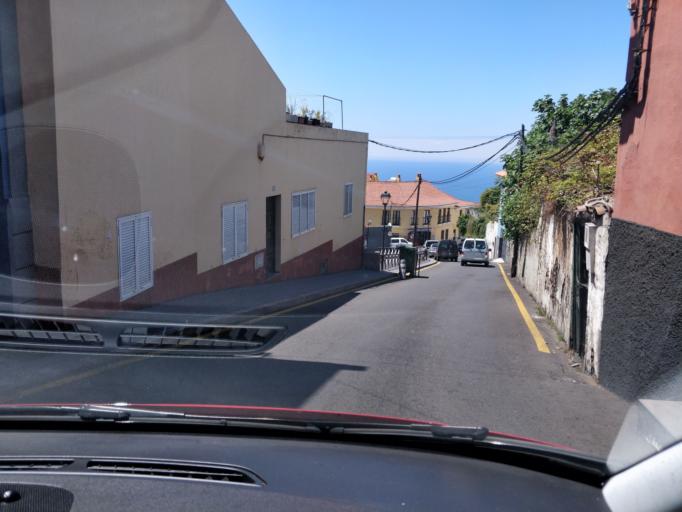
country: ES
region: Canary Islands
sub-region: Provincia de Santa Cruz de Tenerife
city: La Orotava
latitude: 28.3857
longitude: -16.5225
